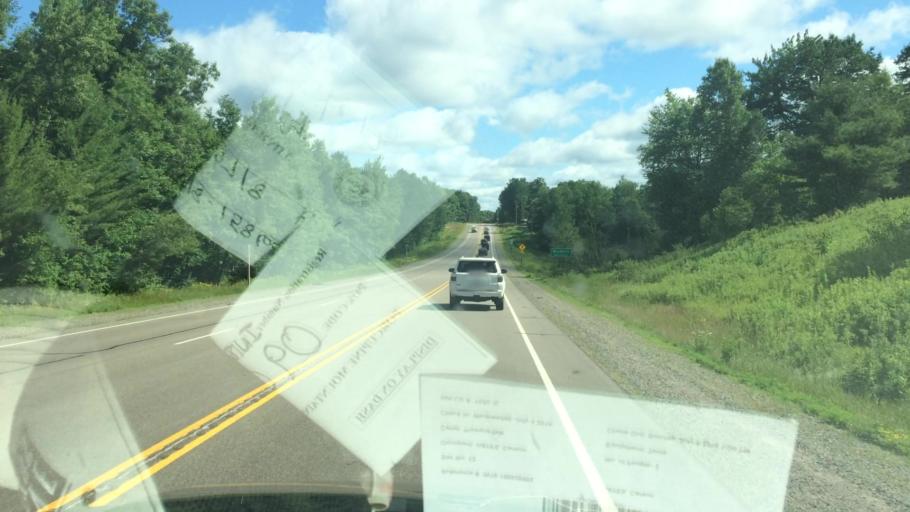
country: US
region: Wisconsin
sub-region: Oneida County
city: Rhinelander
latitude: 45.6015
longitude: -89.5591
